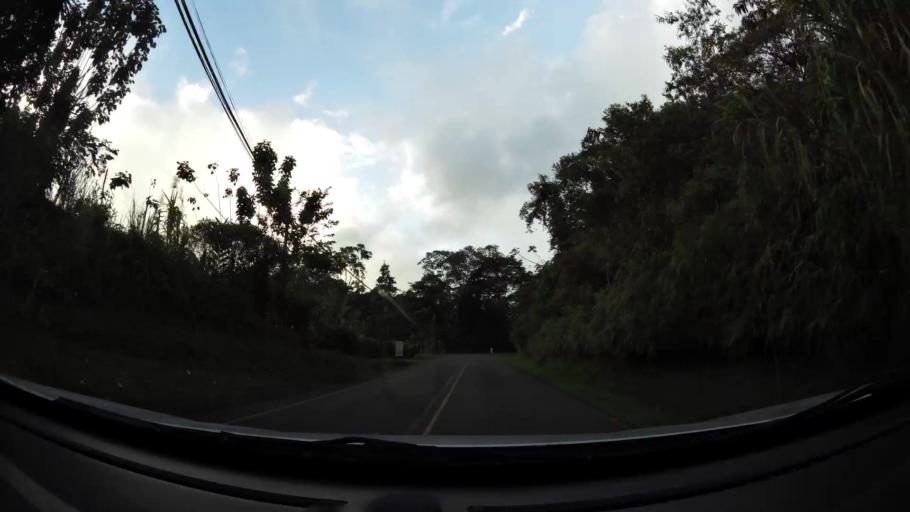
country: CR
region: Cartago
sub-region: Canton de Turrialba
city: La Suiza
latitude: 9.9748
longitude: -83.5698
